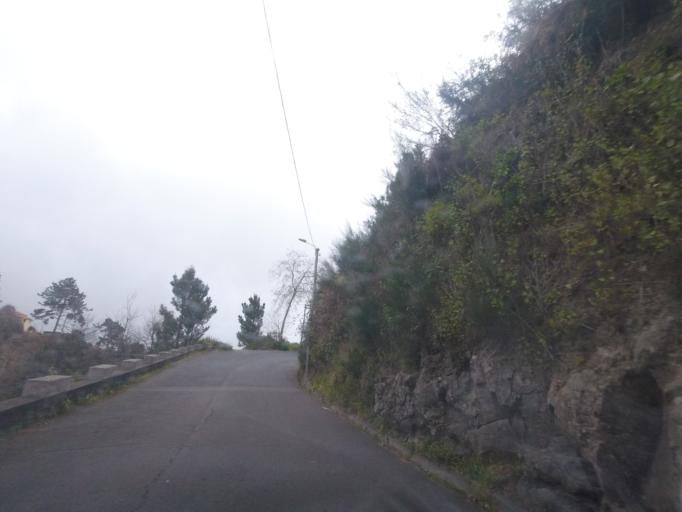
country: PT
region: Madeira
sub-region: Calheta
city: Faja da Ovelha
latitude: 32.7683
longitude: -17.2104
